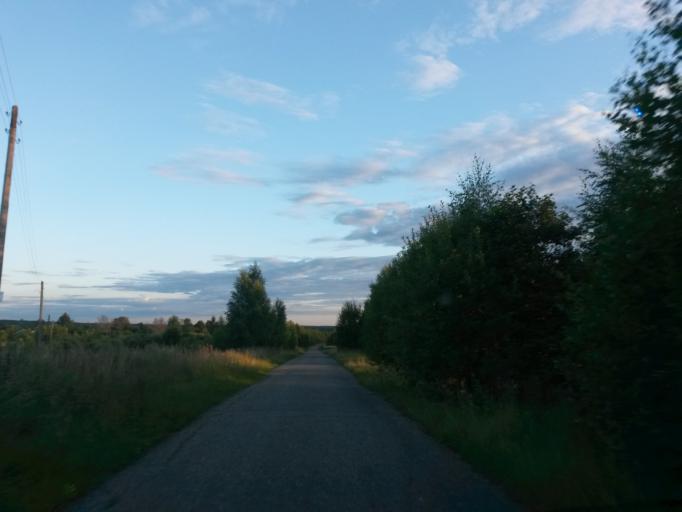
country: RU
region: Jaroslavl
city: Gavrilov-Yam
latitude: 57.3447
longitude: 40.0409
